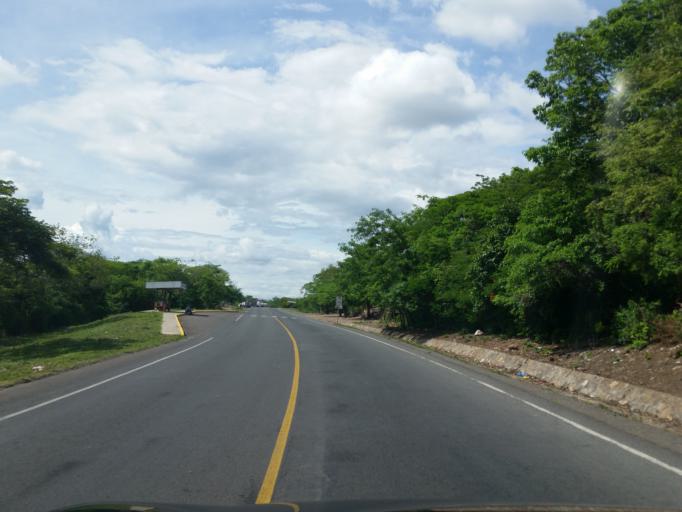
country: NI
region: Matagalpa
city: Ciudad Dario
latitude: 12.5376
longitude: -86.0491
